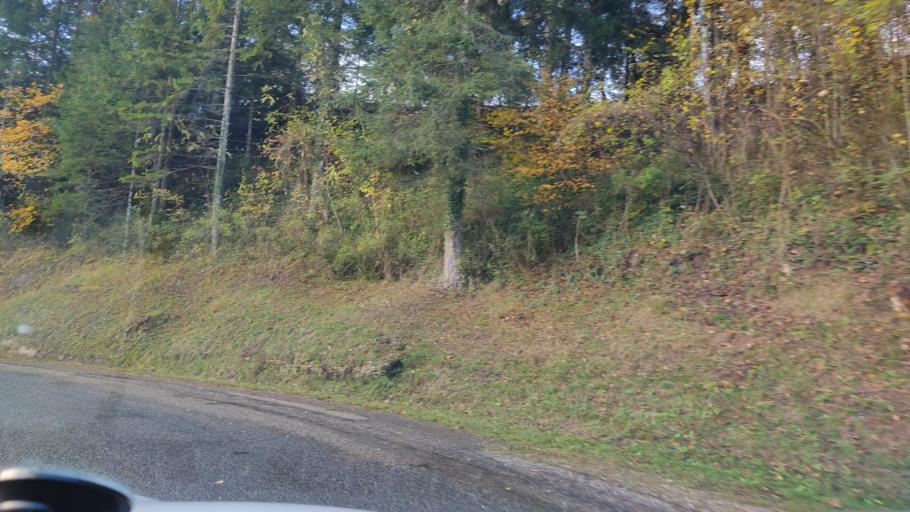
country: FR
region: Rhone-Alpes
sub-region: Departement de la Savoie
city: Novalaise
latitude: 45.6385
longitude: 5.7884
